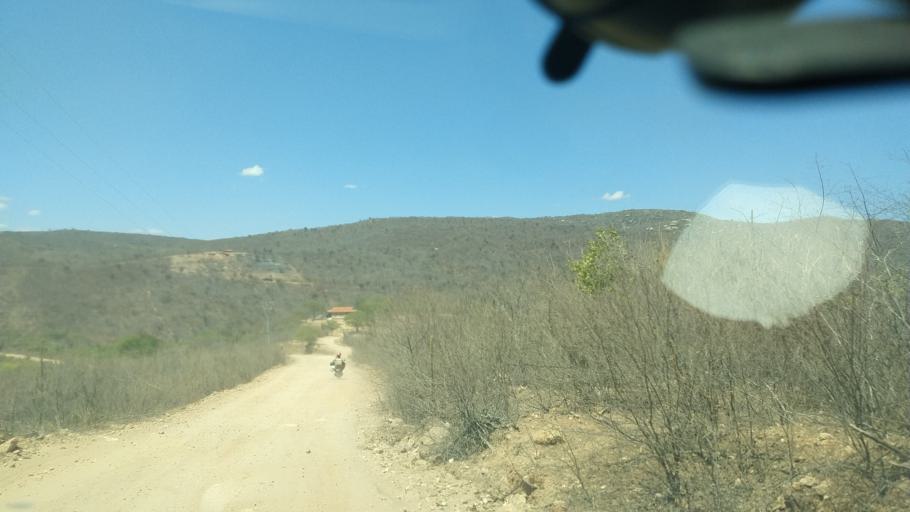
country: BR
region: Rio Grande do Norte
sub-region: Cerro Cora
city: Cerro Cora
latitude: -6.0163
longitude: -36.3076
